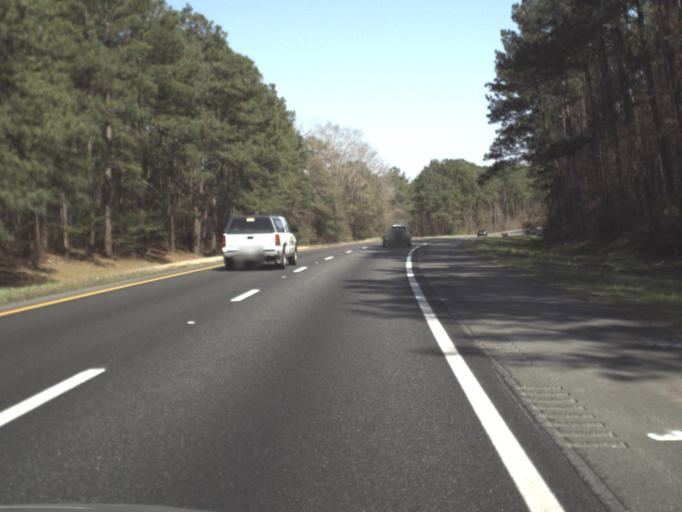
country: US
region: Florida
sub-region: Gadsden County
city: Chattahoochee
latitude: 30.6317
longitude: -84.8749
